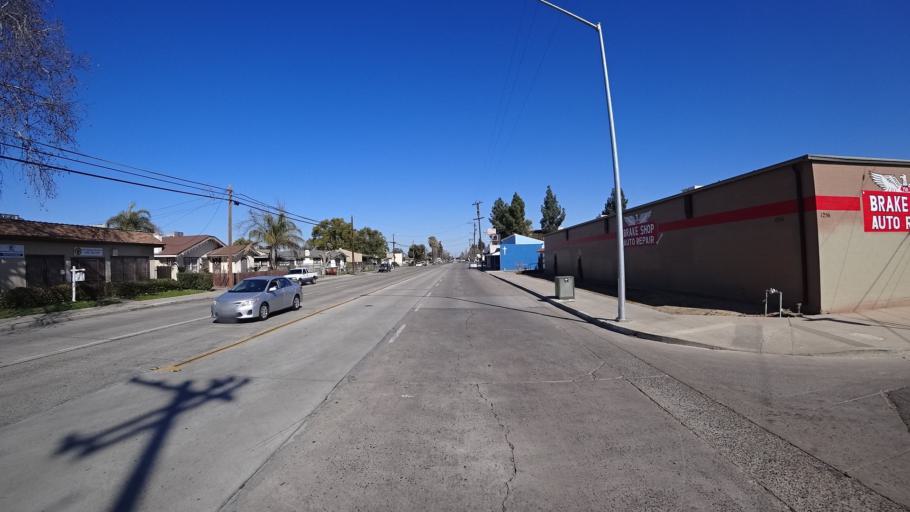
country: US
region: California
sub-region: Fresno County
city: Fresno
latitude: 36.7587
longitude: -119.7815
